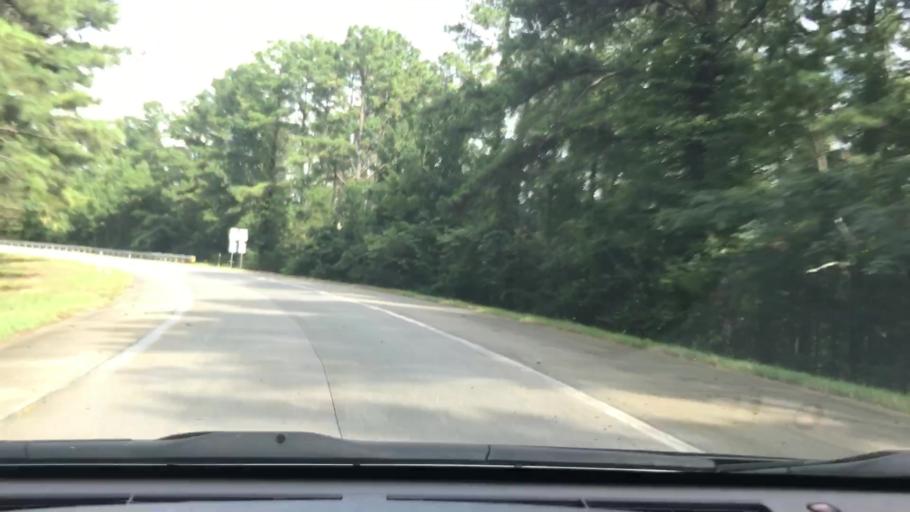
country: US
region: Georgia
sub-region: Taliaferro County
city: Crawfordville
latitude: 33.4971
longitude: -82.8062
